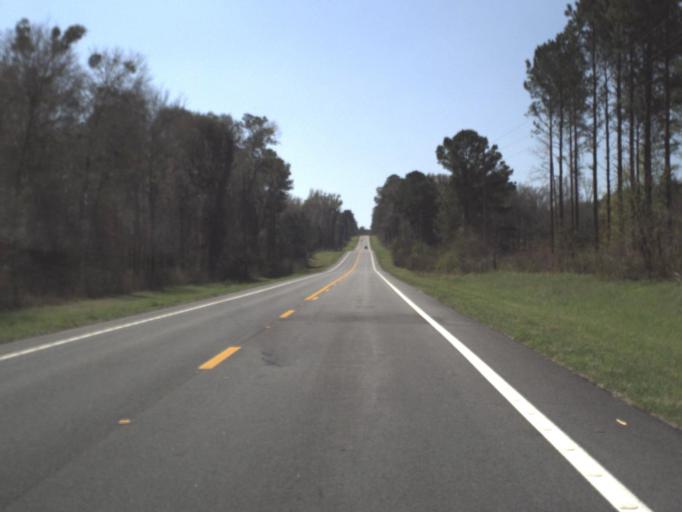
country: US
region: Florida
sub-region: Jefferson County
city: Monticello
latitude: 30.4228
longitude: -84.0201
